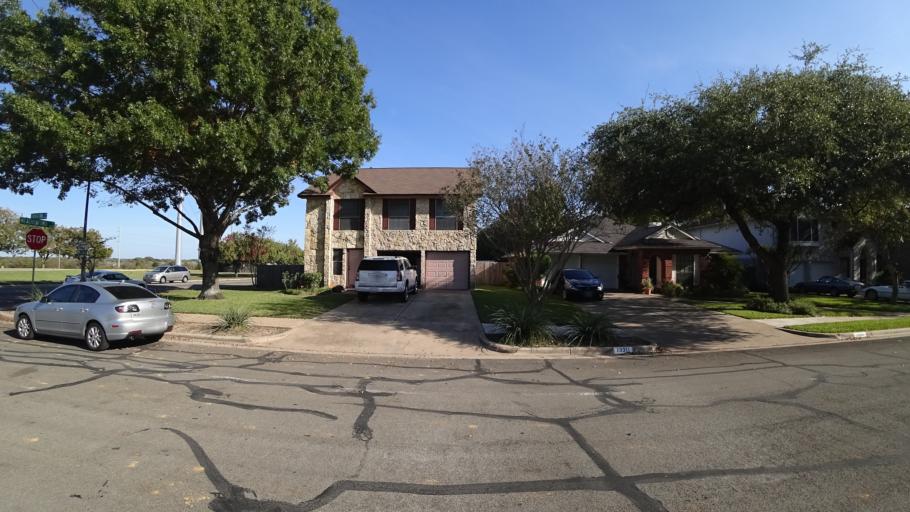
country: US
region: Texas
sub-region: Travis County
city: Pflugerville
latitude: 30.4076
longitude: -97.6491
